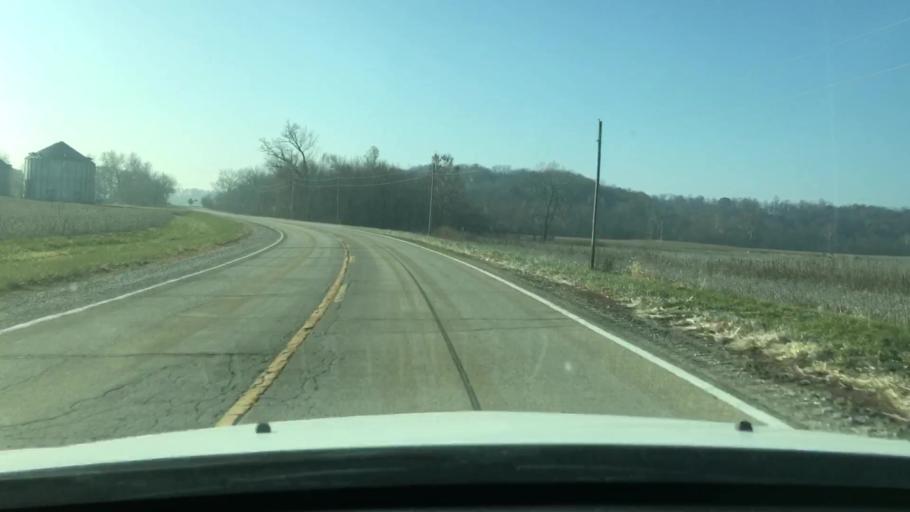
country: US
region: Illinois
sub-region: Mason County
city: Havana
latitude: 40.2770
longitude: -90.1743
